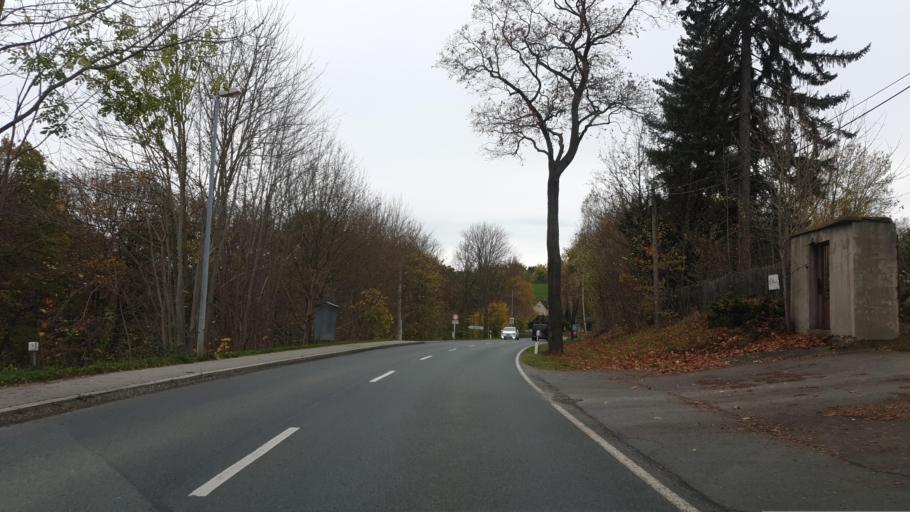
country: DE
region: Saxony
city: Netzschkau
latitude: 50.6093
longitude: 12.2493
